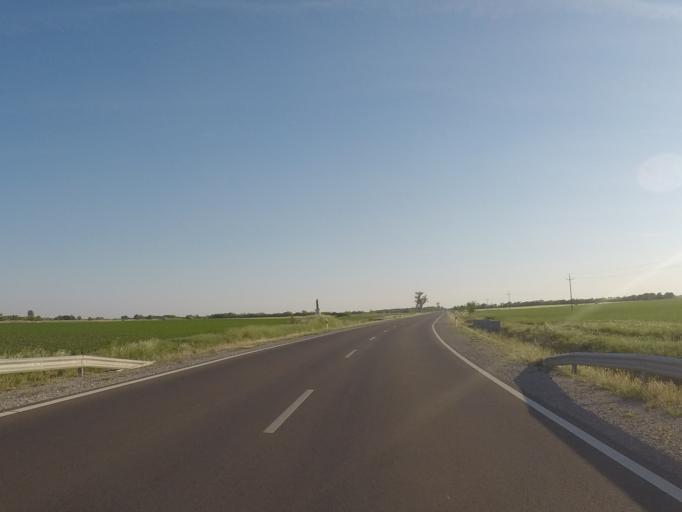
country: HU
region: Heves
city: Besenyotelek
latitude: 47.6837
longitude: 20.3859
